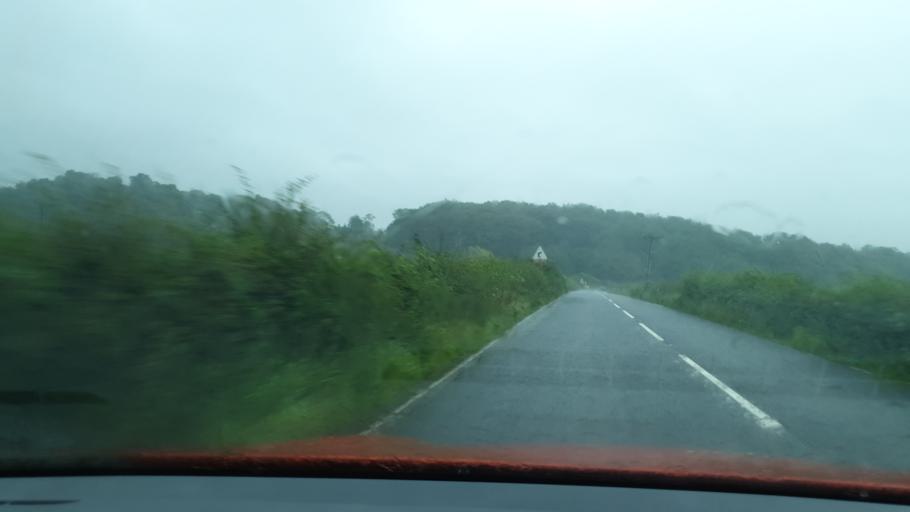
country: GB
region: England
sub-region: Cumbria
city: Millom
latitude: 54.2700
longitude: -3.2193
